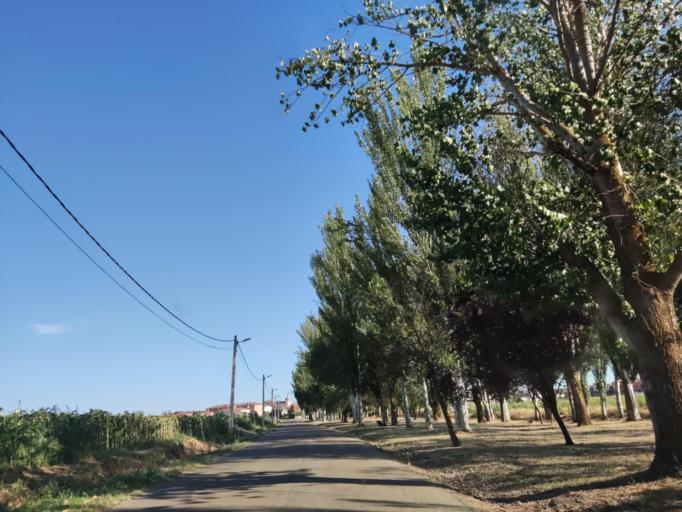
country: ES
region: Castille and Leon
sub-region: Provincia de Zamora
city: Villaralbo
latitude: 41.4976
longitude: -5.6854
